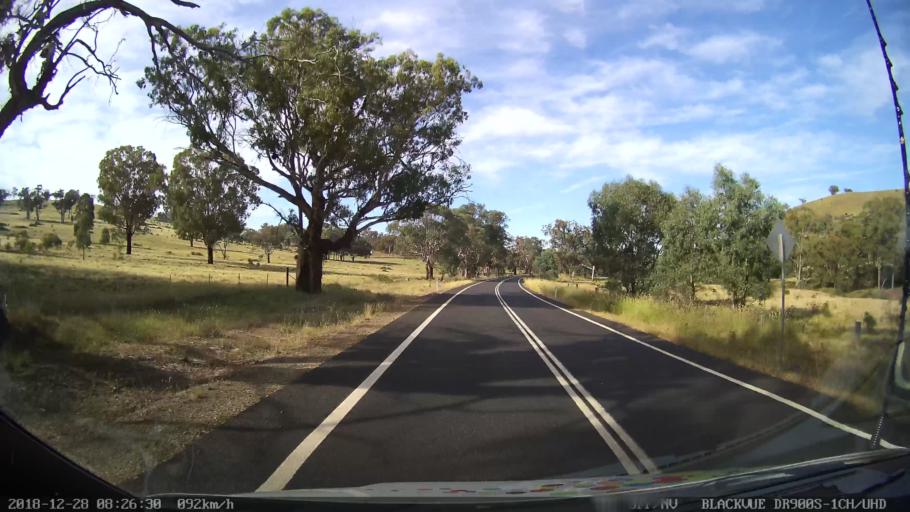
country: AU
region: New South Wales
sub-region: Blayney
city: Blayney
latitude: -33.9366
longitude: 149.3470
